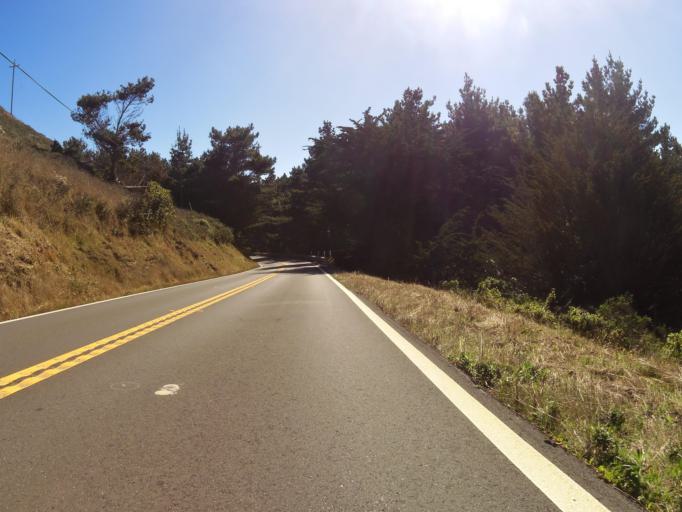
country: US
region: California
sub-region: Mendocino County
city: Fort Bragg
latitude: 39.6023
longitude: -123.7856
